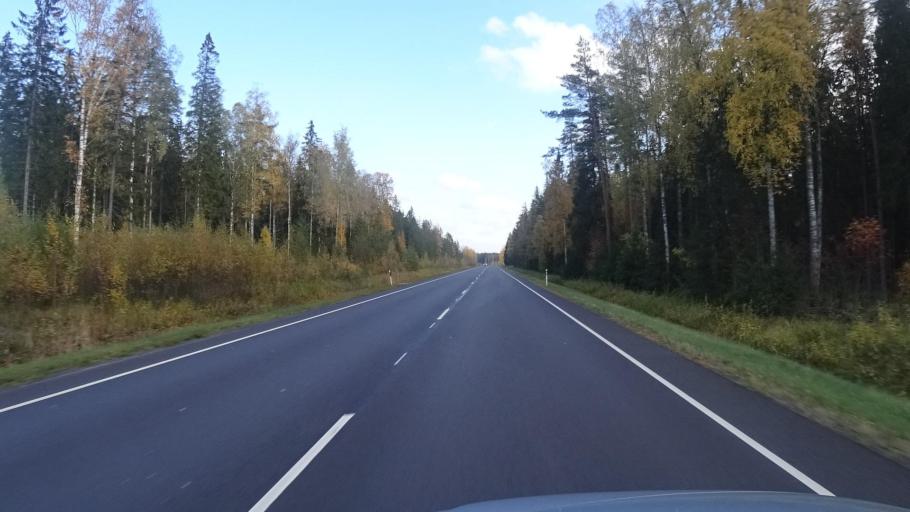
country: FI
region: Satakunta
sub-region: Rauma
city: Eura
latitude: 61.1128
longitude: 22.2017
